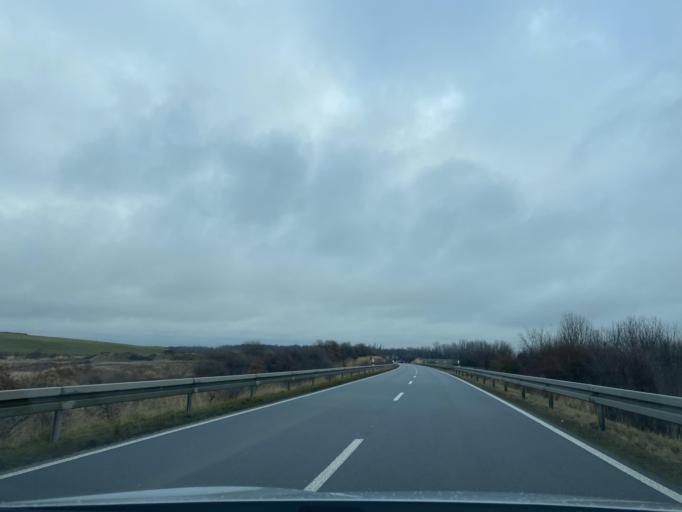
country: DE
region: Saxony
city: Kodersdorf
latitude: 51.2121
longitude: 14.9407
